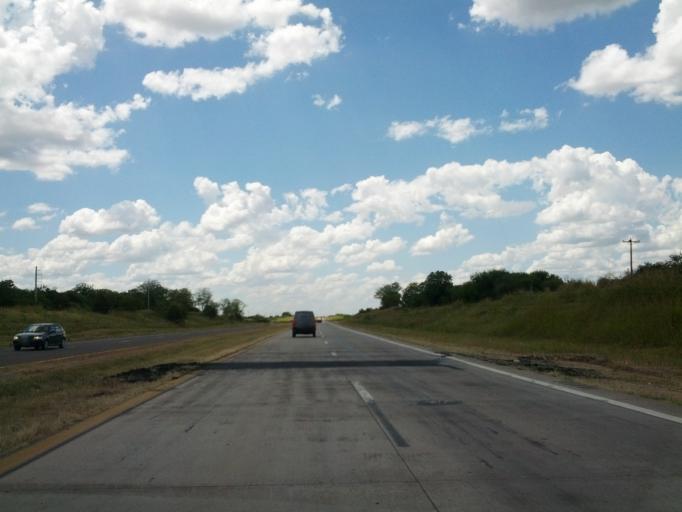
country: AR
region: Entre Rios
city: Gualeguaychu
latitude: -32.9446
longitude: -58.5776
